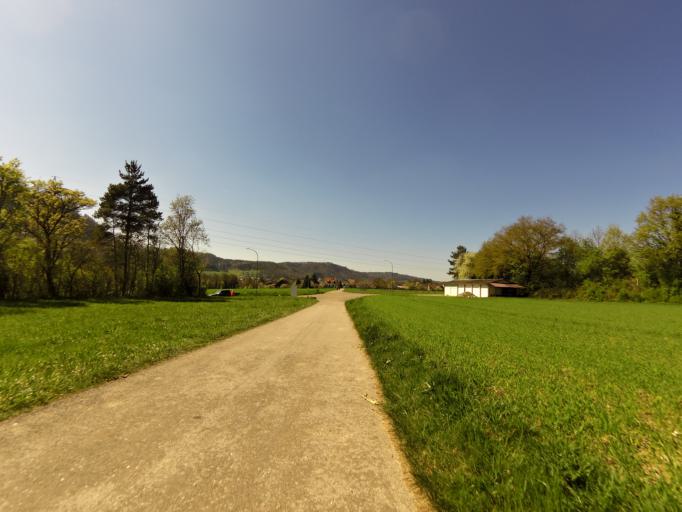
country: CH
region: Aargau
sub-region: Bezirk Zurzach
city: Bad Zurzach
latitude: 47.5716
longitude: 8.3375
